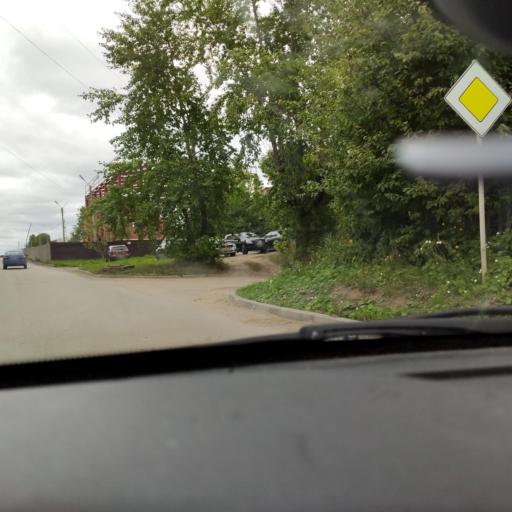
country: RU
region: Perm
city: Dobryanka
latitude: 58.4612
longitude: 56.3983
